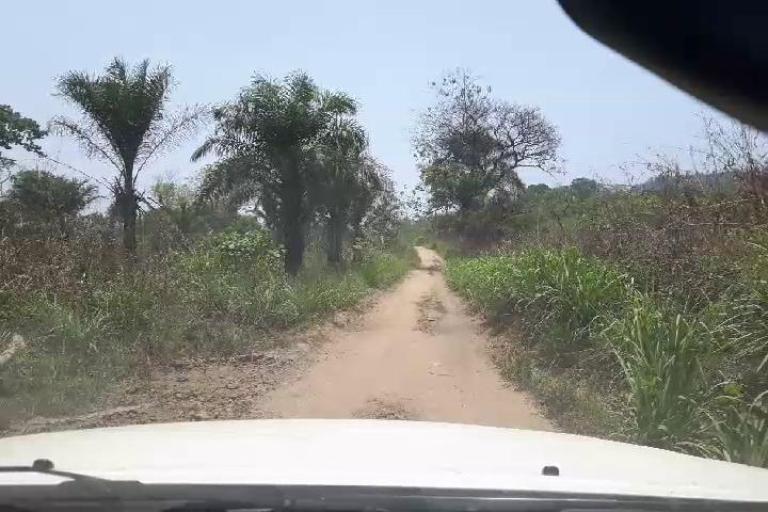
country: SL
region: Northern Province
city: Alikalia
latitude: 9.0856
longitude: -11.4649
